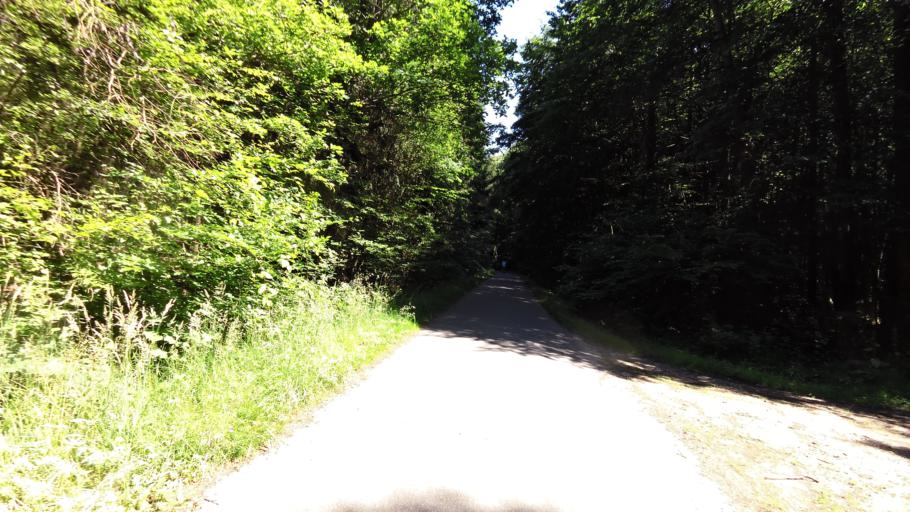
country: DE
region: North Rhine-Westphalia
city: Meckenheim
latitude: 50.6618
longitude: 7.0330
